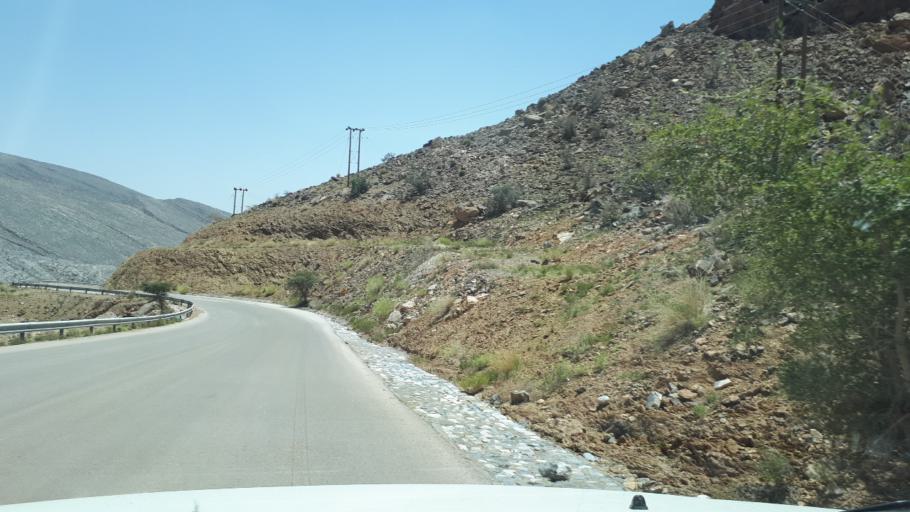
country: OM
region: Muhafazat ad Dakhiliyah
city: Bahla'
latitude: 23.2224
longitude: 57.1445
